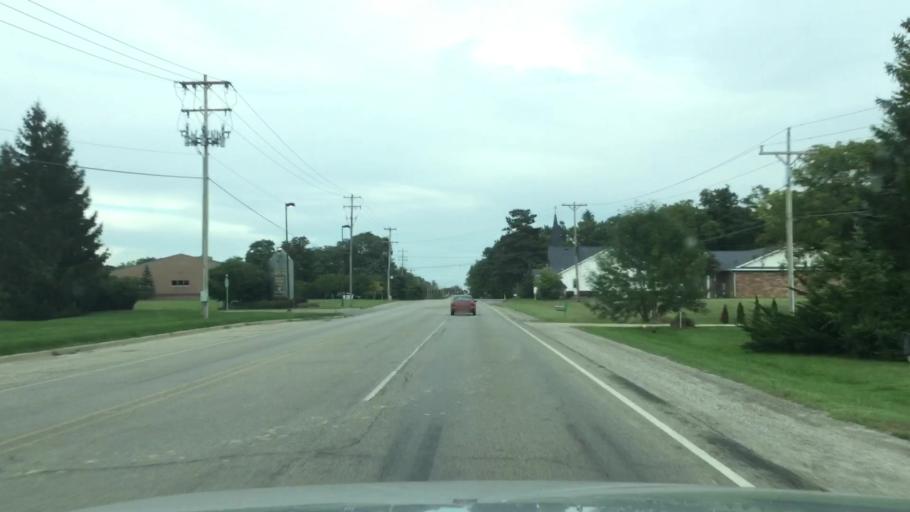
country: US
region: Michigan
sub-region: Genesee County
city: Grand Blanc
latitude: 42.8866
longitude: -83.6414
